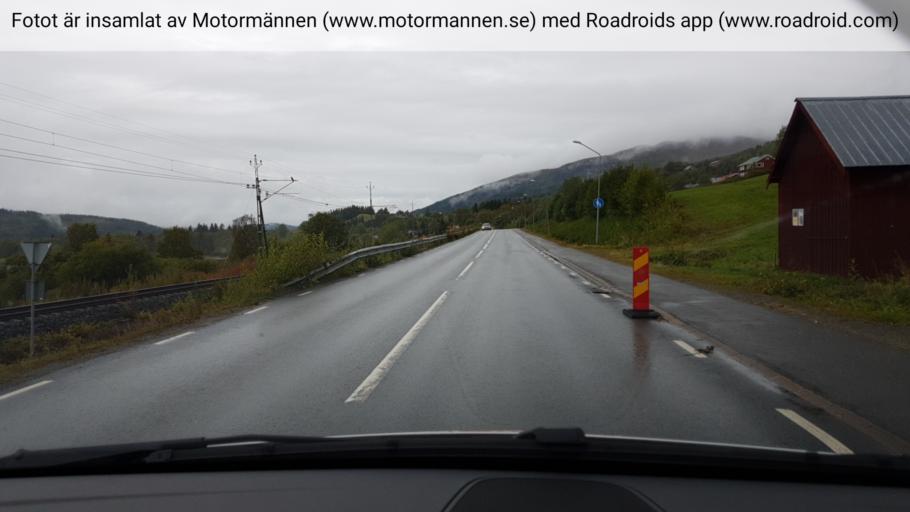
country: SE
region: Jaemtland
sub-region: Are Kommun
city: Are
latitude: 63.4034
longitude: 13.0465
